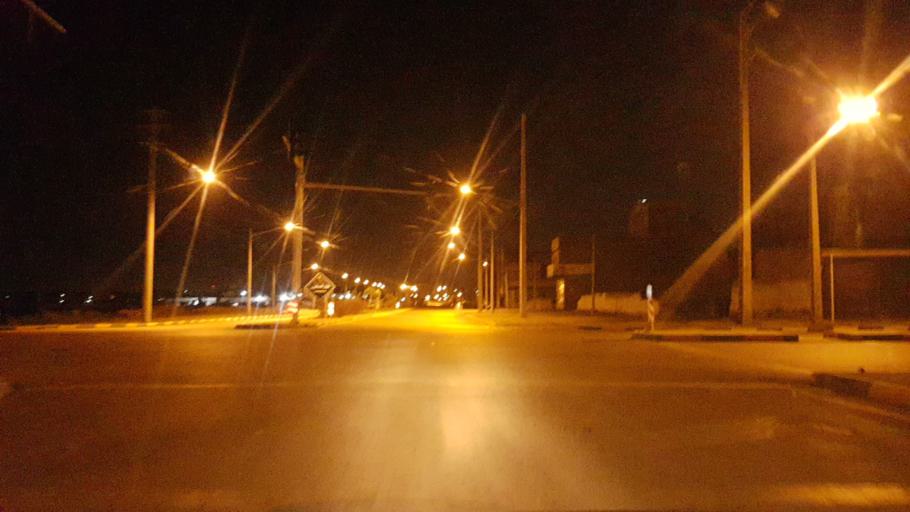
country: IR
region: Razavi Khorasan
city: Mashhad
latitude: 36.3561
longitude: 59.5662
